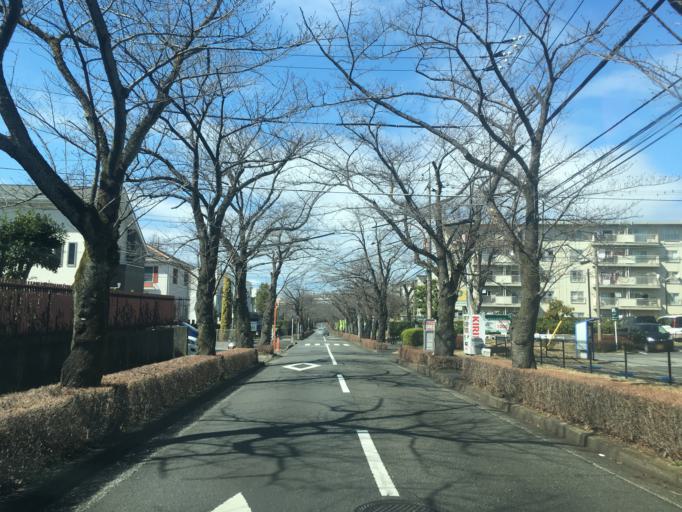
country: JP
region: Tokyo
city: Hino
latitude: 35.6182
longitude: 139.4490
